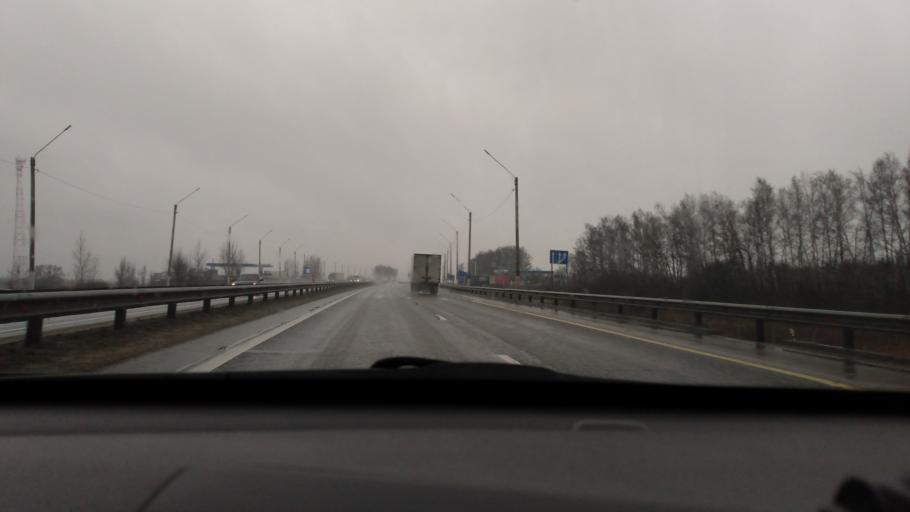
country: RU
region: Tula
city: Venev
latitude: 54.4375
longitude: 38.1836
